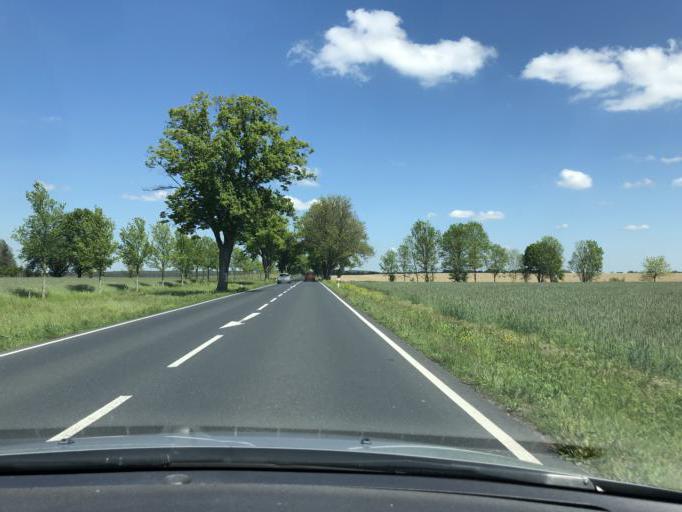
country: DE
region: Brandenburg
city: Herzberg
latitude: 51.7194
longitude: 13.2894
